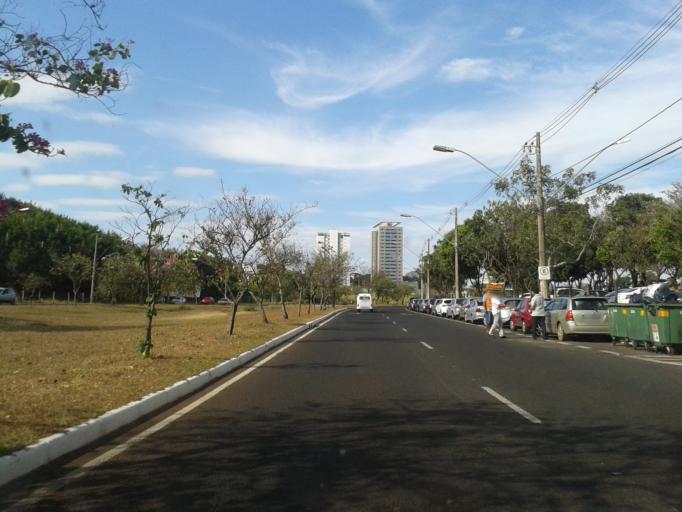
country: BR
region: Minas Gerais
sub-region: Uberlandia
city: Uberlandia
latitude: -18.9113
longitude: -48.2557
